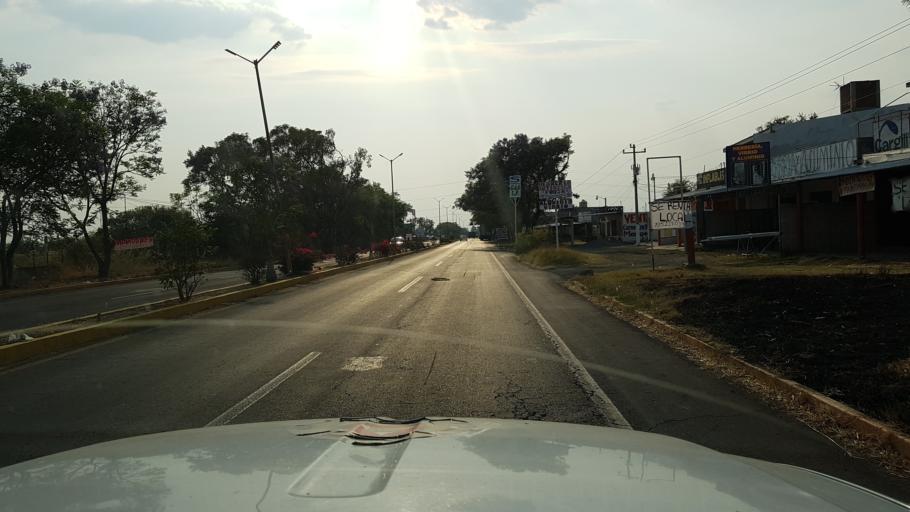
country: MX
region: Morelos
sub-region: Yecapixtla
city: Yecapixtla
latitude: 18.8897
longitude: -98.8827
